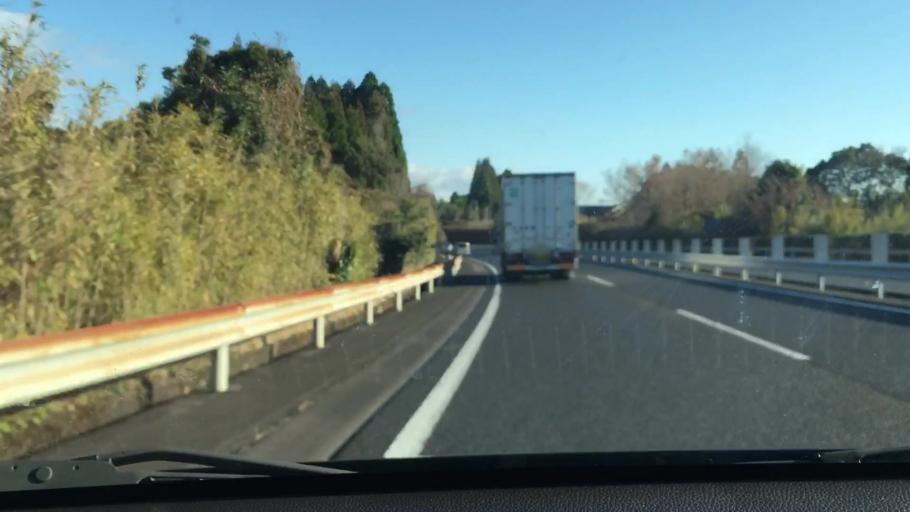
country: JP
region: Kagoshima
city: Kajiki
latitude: 31.8215
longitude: 130.6953
